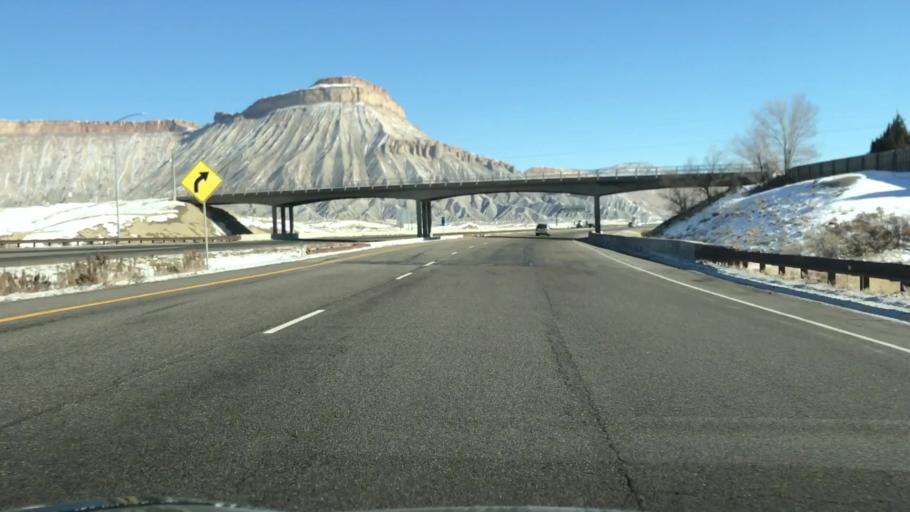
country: US
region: Colorado
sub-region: Mesa County
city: Clifton
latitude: 39.1065
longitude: -108.4419
